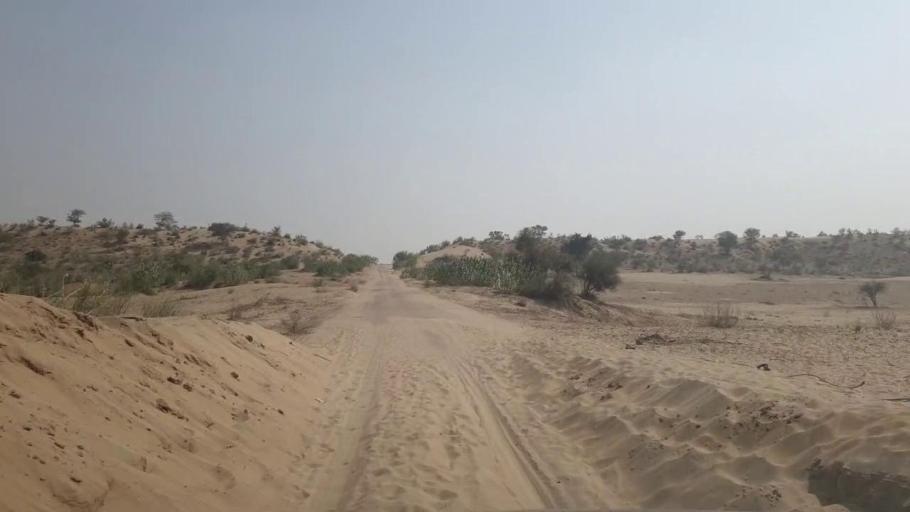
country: PK
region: Sindh
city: Chor
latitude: 25.5920
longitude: 70.0047
